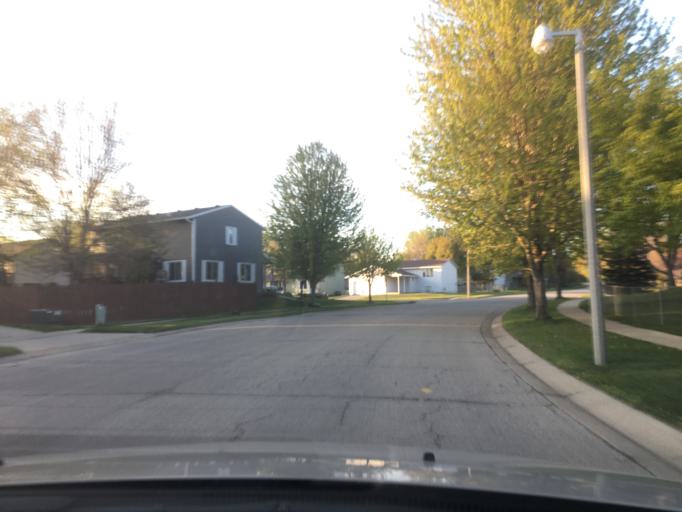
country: US
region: Minnesota
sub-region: Olmsted County
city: Rochester
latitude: 44.0813
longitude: -92.5289
